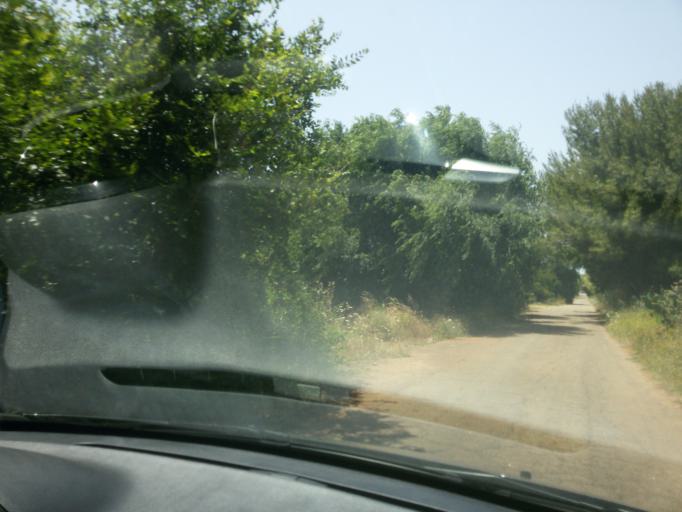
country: IT
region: Apulia
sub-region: Provincia di Lecce
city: Porto Cesareo
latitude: 40.3258
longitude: 17.8603
